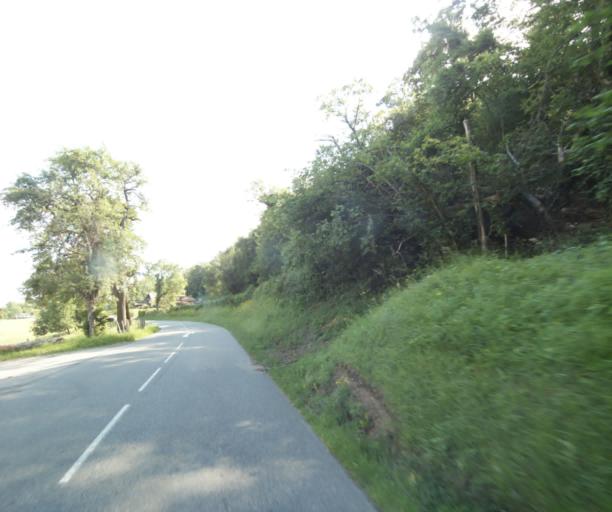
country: FR
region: Rhone-Alpes
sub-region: Departement de la Haute-Savoie
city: Lyaud
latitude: 46.3158
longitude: 6.4978
